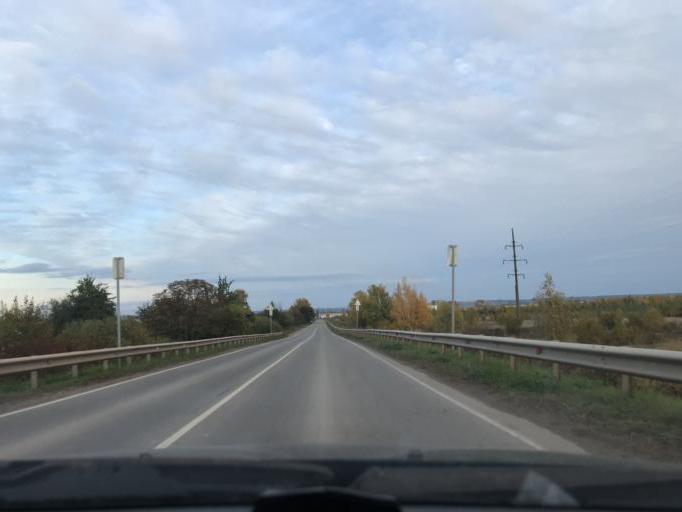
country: RU
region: Kaluga
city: Kurovskoye
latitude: 54.5278
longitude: 35.9988
